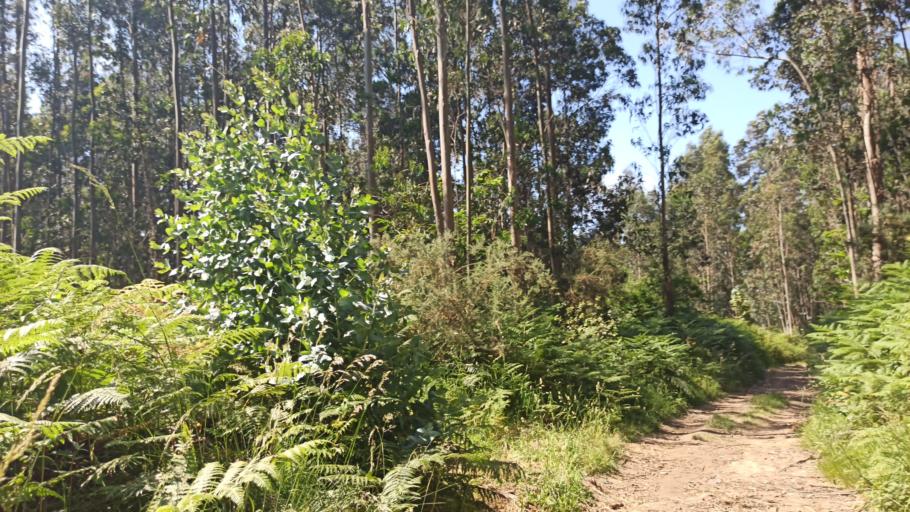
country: ES
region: Galicia
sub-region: Provincia da Coruna
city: Sada
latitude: 43.3808
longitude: -8.2711
